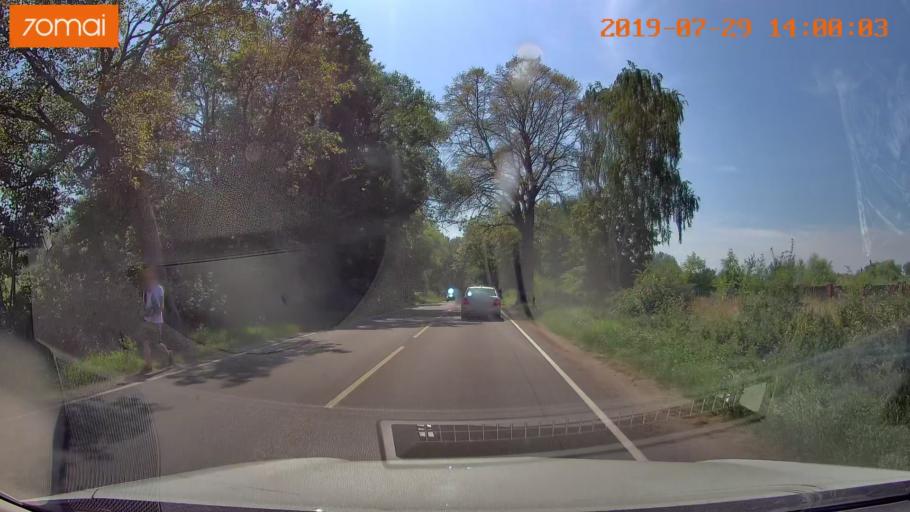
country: RU
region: Kaliningrad
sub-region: Gorod Kaliningrad
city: Baltiysk
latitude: 54.6815
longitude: 19.9300
